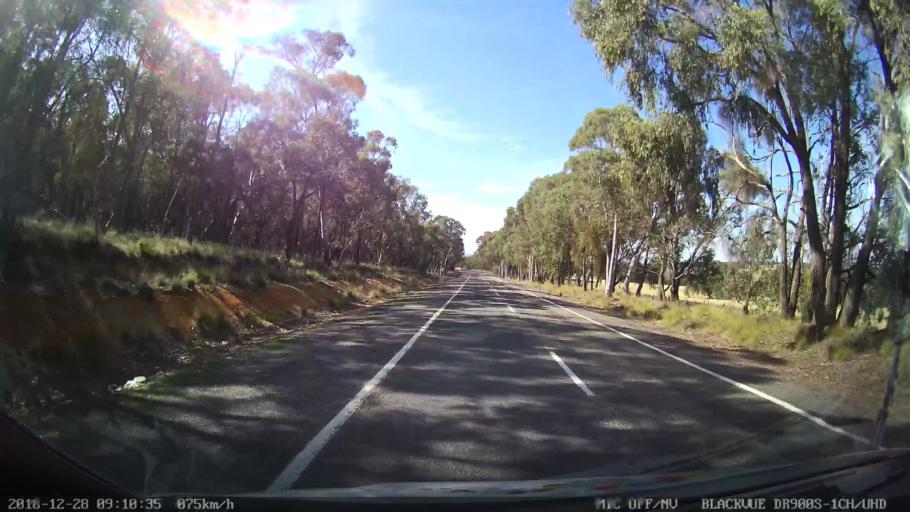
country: AU
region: New South Wales
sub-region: Upper Lachlan Shire
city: Crookwell
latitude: -34.2335
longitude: 149.3367
